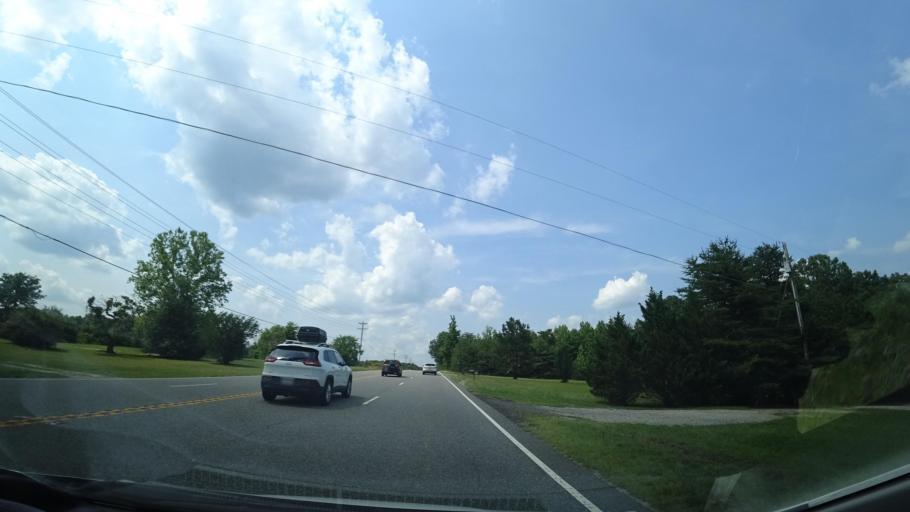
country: US
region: Virginia
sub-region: Hanover County
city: Ashland
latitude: 37.9215
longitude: -77.4776
